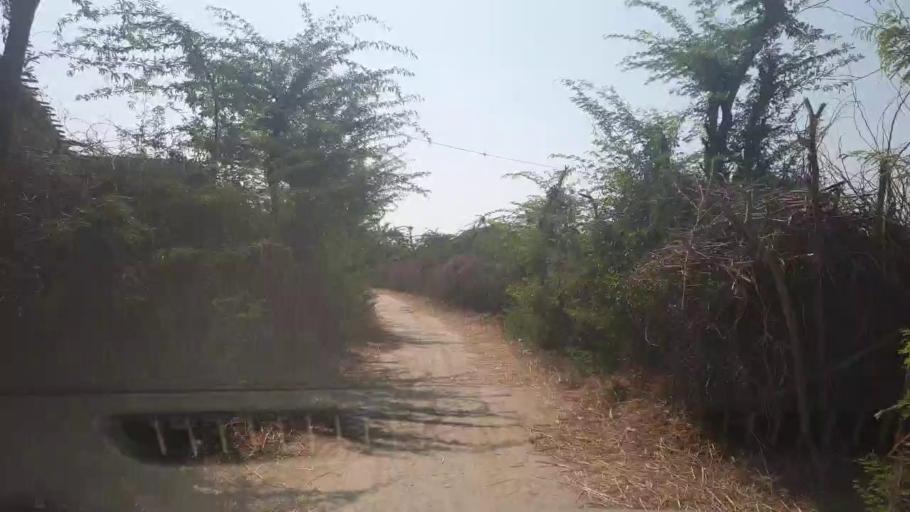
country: PK
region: Sindh
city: Badin
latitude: 24.6283
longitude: 68.9104
